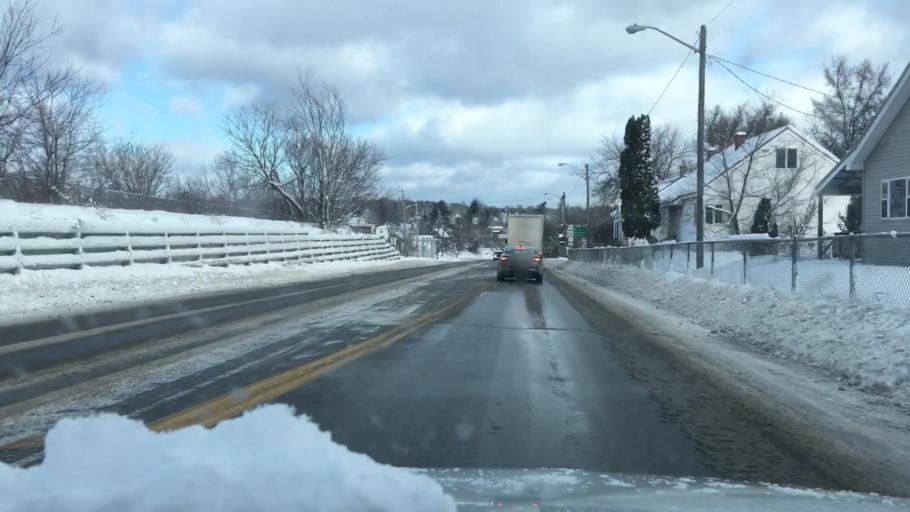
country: US
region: Maine
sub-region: Aroostook County
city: Caribou
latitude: 46.8525
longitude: -68.0055
